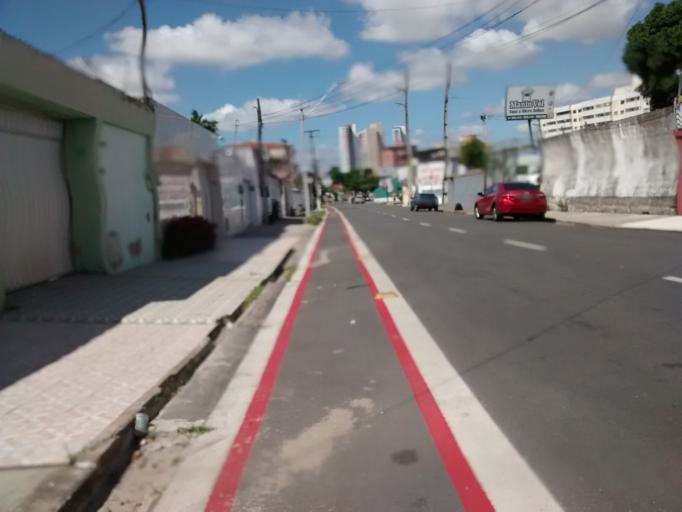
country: BR
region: Ceara
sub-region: Fortaleza
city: Fortaleza
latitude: -3.7295
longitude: -38.5603
